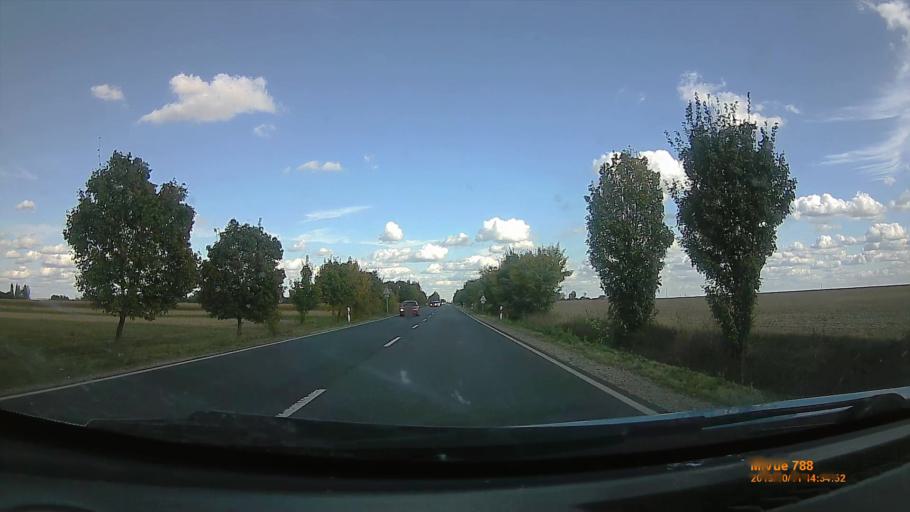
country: HU
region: Hajdu-Bihar
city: Ebes
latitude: 47.5600
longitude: 21.4826
